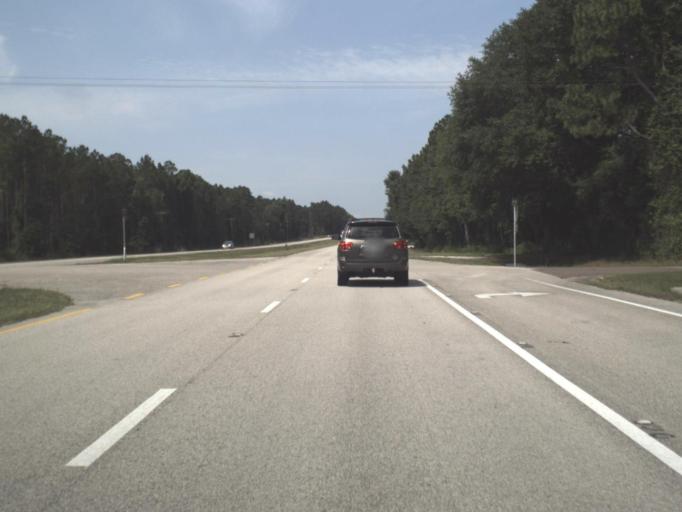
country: US
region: Florida
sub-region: Alachua County
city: Waldo
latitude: 29.7459
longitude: -82.2280
